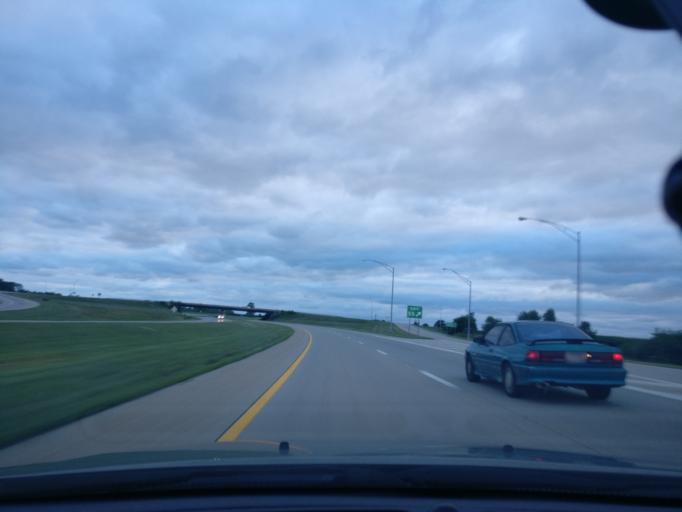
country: US
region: Ohio
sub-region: Greene County
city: Wilberforce
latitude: 39.6912
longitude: -83.8795
